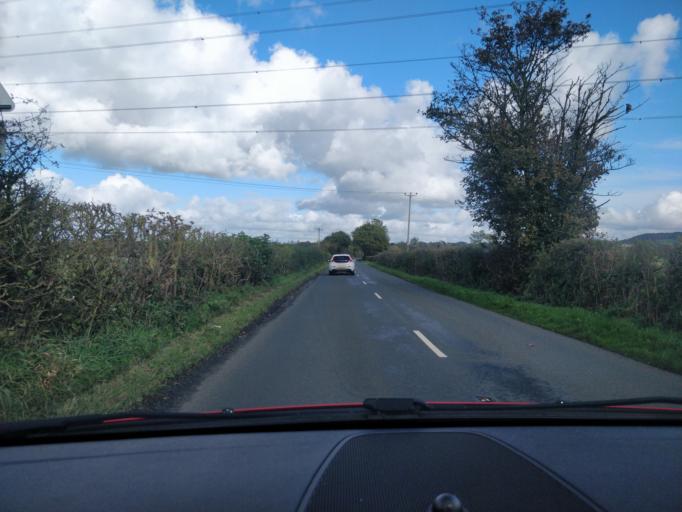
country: GB
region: England
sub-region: Lancashire
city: Parbold
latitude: 53.6078
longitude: -2.7913
